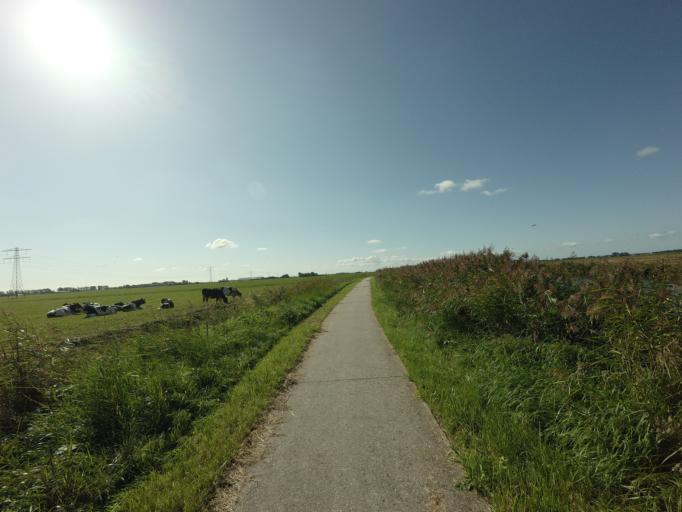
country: NL
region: Friesland
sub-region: Gemeente Boarnsterhim
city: Reduzum
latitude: 53.1432
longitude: 5.7644
